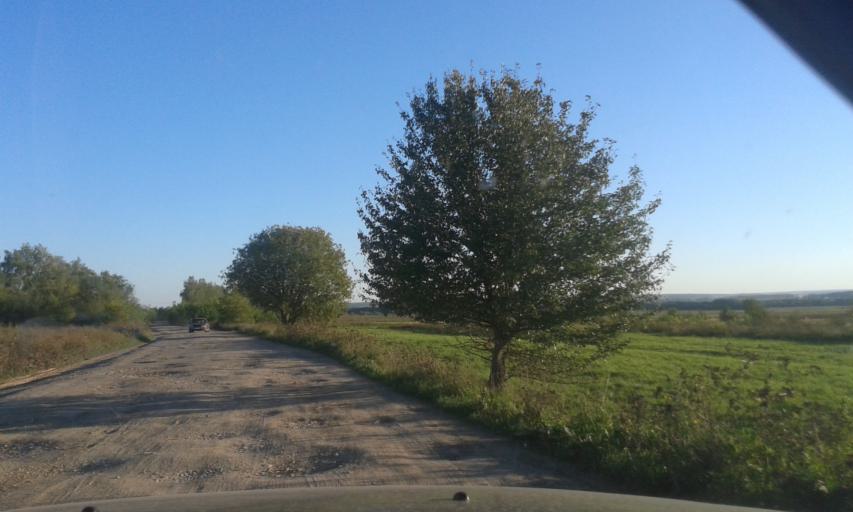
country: RU
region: Tula
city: Krapivna
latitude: 54.1343
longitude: 37.1572
